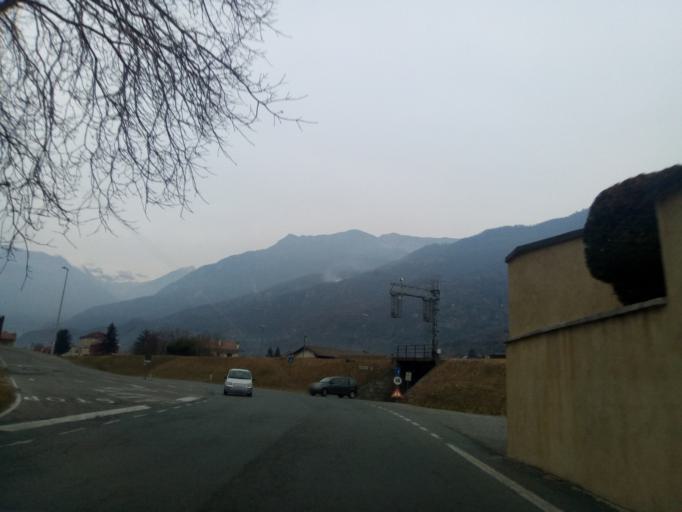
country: IT
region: Piedmont
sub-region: Provincia di Torino
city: Tavagnasco
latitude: 45.5438
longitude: 7.8261
